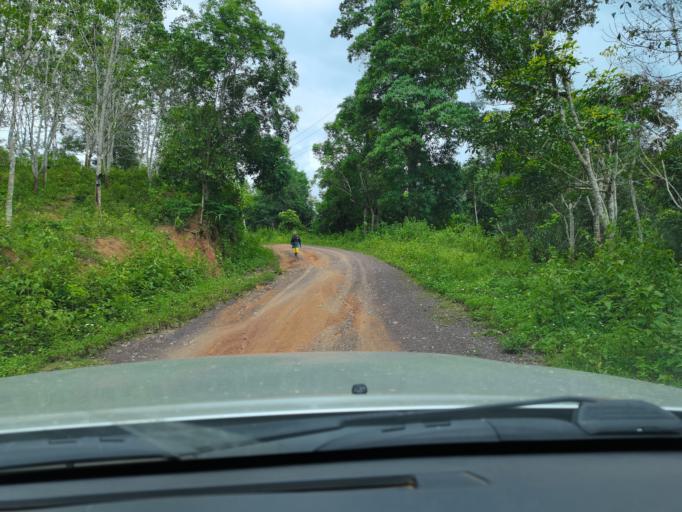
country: LA
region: Loungnamtha
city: Muang Long
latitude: 20.7007
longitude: 101.0217
